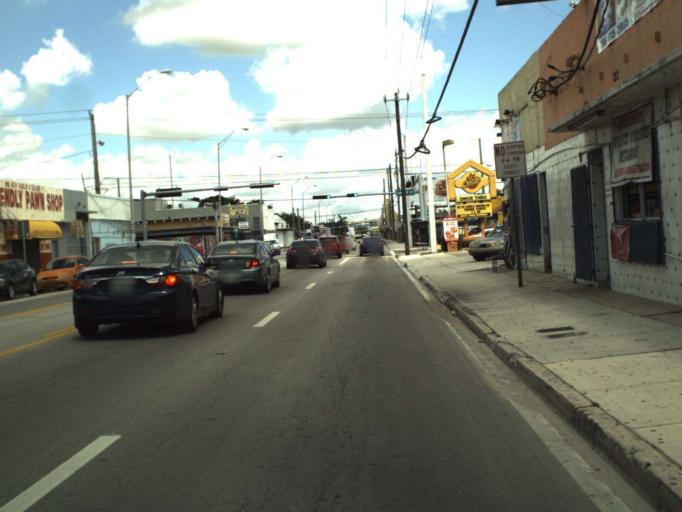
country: US
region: Florida
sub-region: Miami-Dade County
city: Allapattah
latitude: 25.8029
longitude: -80.2072
